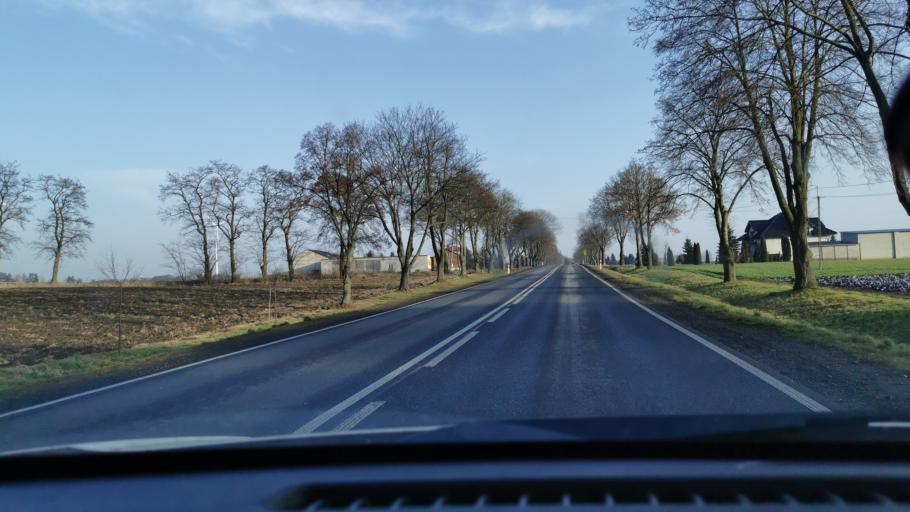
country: PL
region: Lodz Voivodeship
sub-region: Powiat sieradzki
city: Wroblew
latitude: 51.6355
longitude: 18.5293
